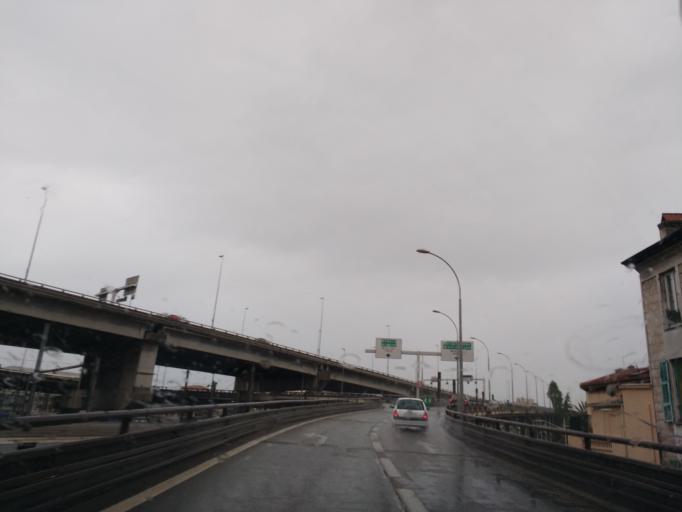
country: FR
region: Provence-Alpes-Cote d'Azur
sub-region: Departement des Alpes-Maritimes
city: Nice
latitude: 43.7047
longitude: 7.2576
